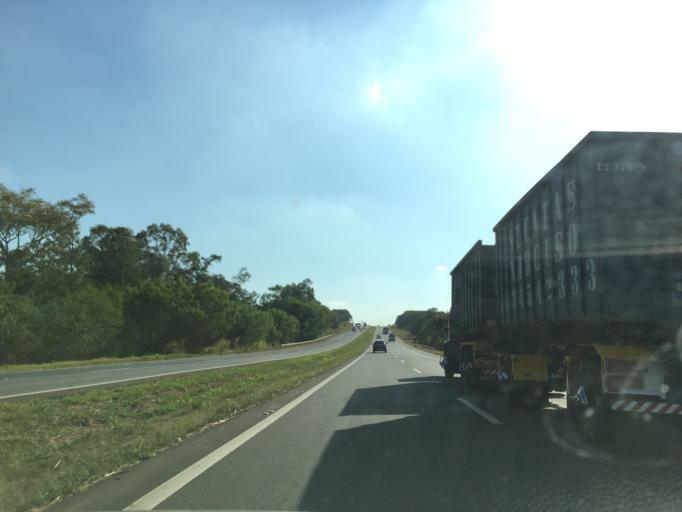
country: BR
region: Sao Paulo
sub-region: Piracicaba
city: Piracicaba
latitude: -22.7263
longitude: -47.5609
